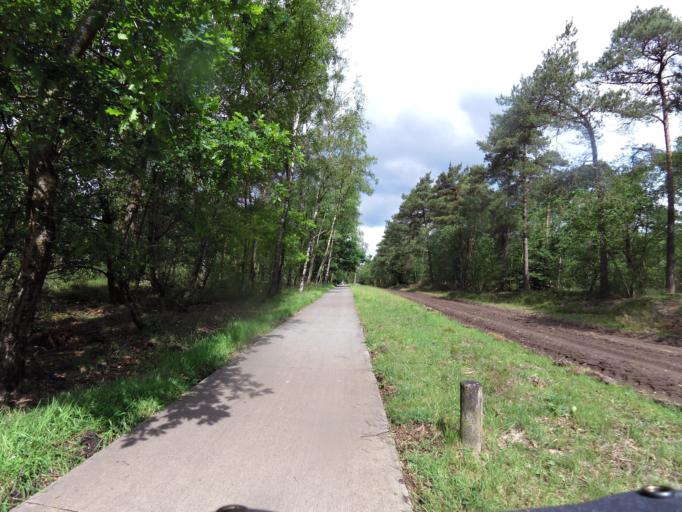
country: NL
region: Gelderland
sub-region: Gemeente Apeldoorn
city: Uddel
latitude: 52.3097
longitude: 5.7691
